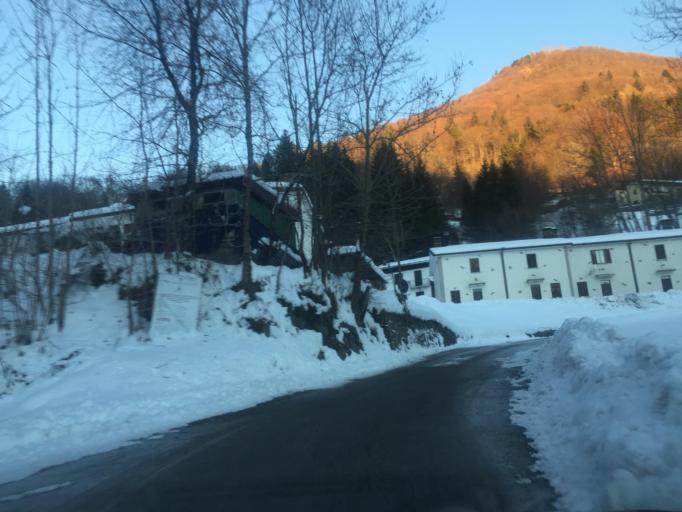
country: IT
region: Friuli Venezia Giulia
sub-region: Provincia di Udine
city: Lauco
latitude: 46.4400
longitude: 12.9442
